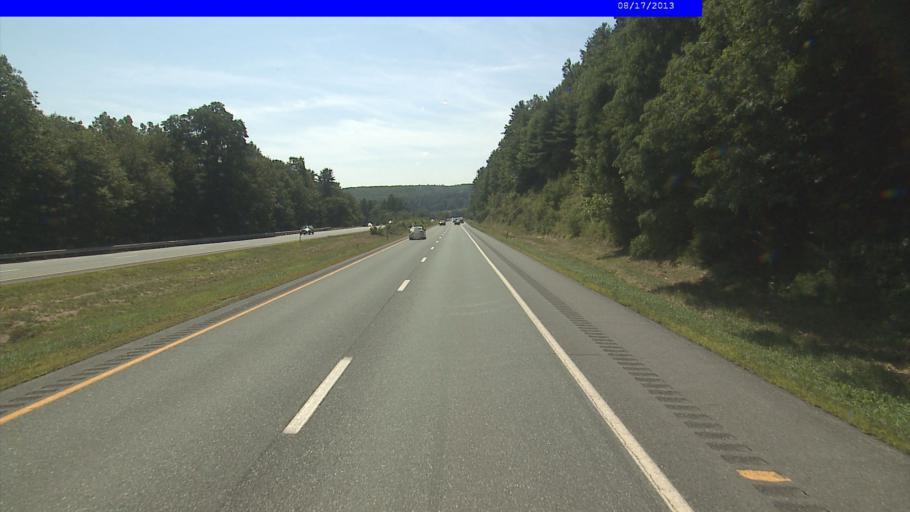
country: US
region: Vermont
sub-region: Windham County
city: Brattleboro
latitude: 42.8408
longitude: -72.5707
